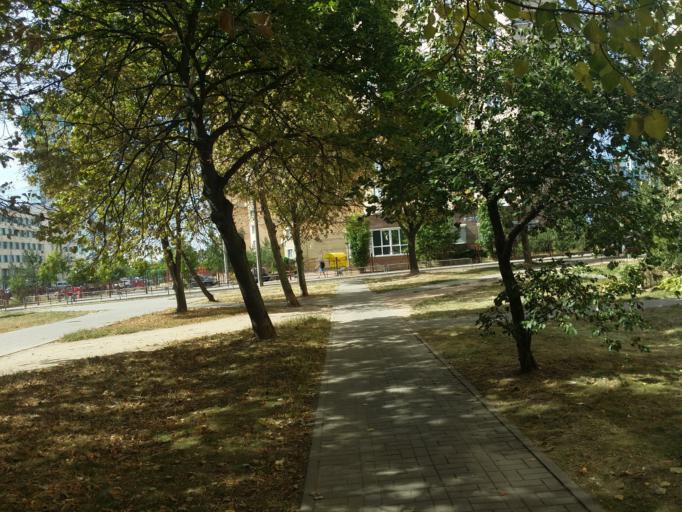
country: BY
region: Minsk
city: Minsk
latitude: 53.9407
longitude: 27.6008
